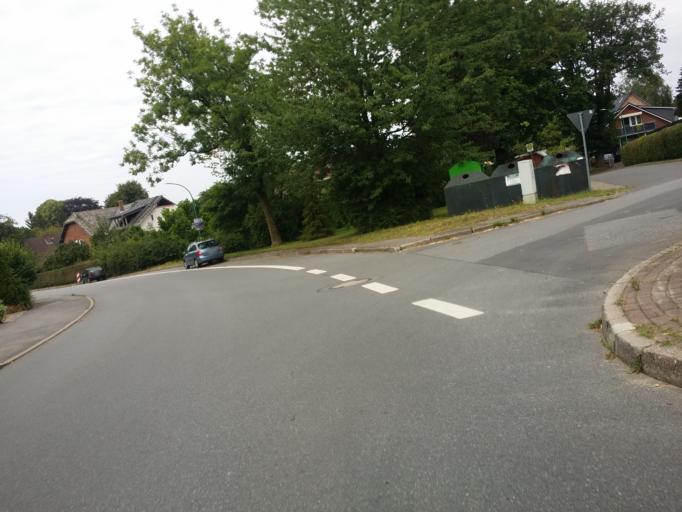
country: DE
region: Schleswig-Holstein
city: Oldendorf
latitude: 53.9534
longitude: 9.4586
